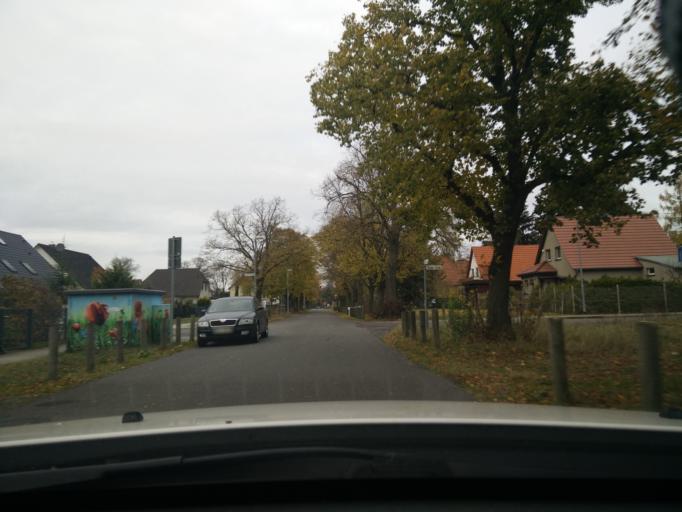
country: DE
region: Berlin
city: Staaken
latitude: 52.5545
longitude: 13.1428
